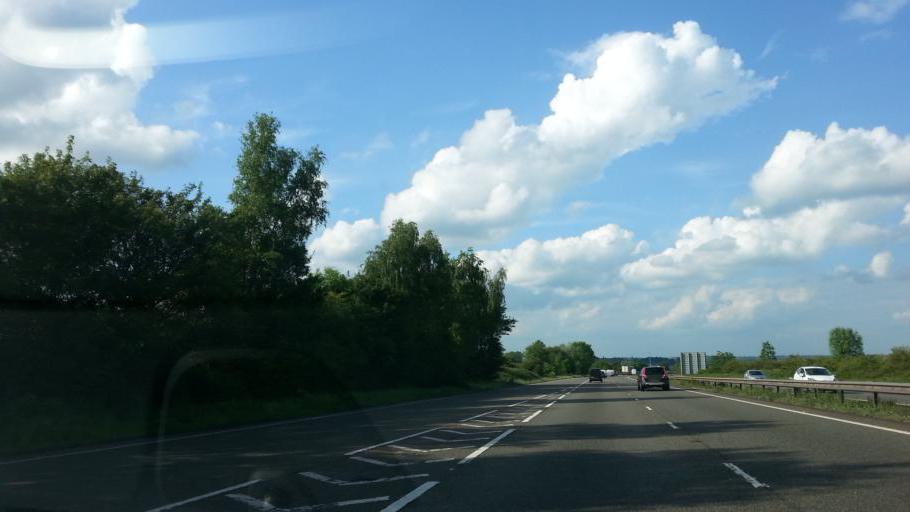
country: GB
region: England
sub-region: Leicestershire
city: Donisthorpe
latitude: 52.6926
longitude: -1.5473
